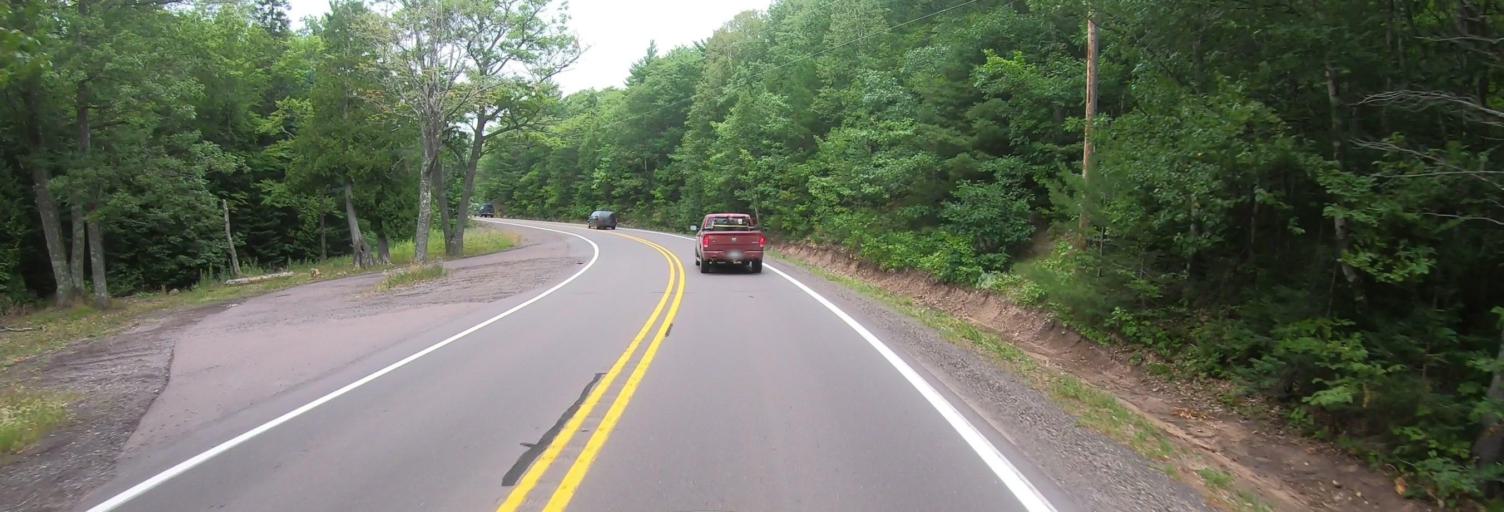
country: US
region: Michigan
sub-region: Keweenaw County
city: Eagle River
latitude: 47.4301
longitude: -87.9828
